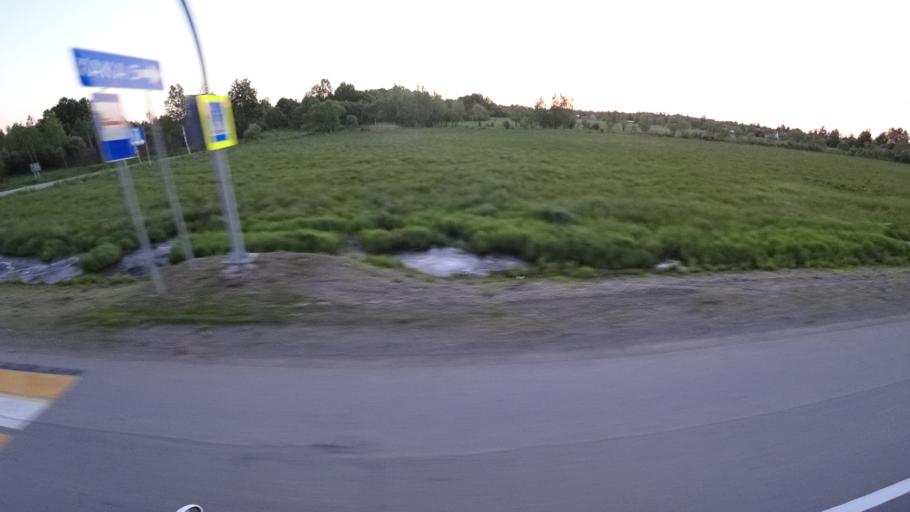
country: RU
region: Khabarovsk Krai
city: Khor
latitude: 47.8424
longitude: 134.9567
